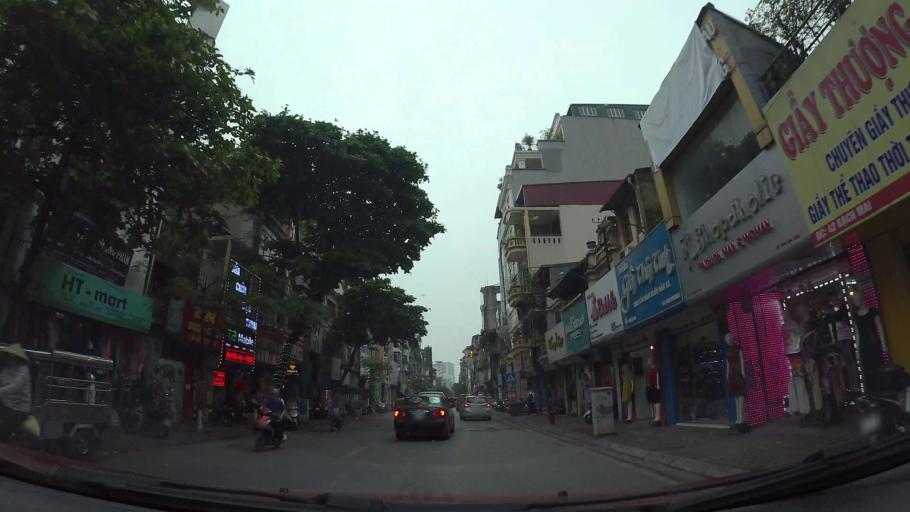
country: VN
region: Ha Noi
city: Hai BaTrung
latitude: 21.0076
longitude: 105.8513
